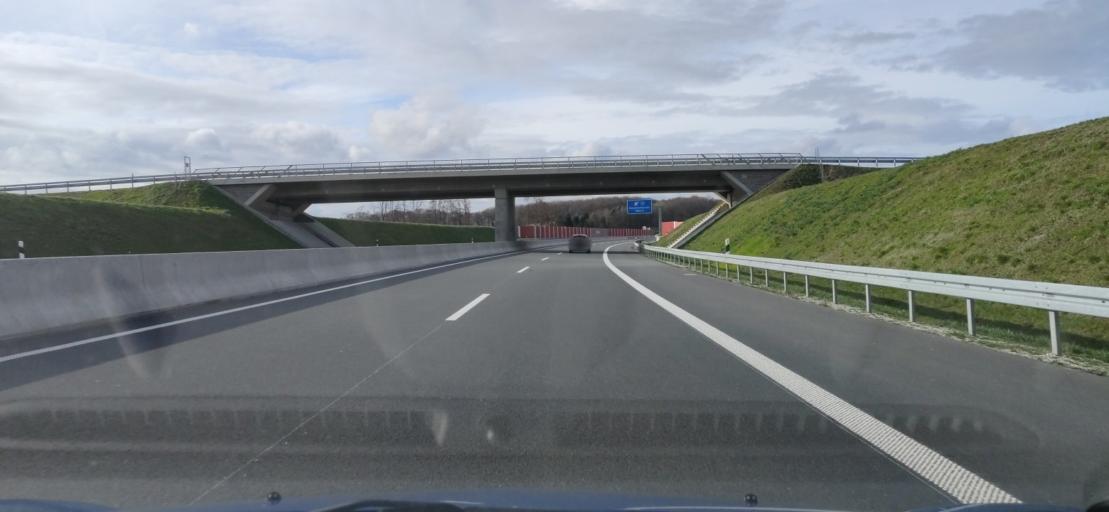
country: DE
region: North Rhine-Westphalia
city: Borgholzhausen
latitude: 52.0684
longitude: 8.2635
